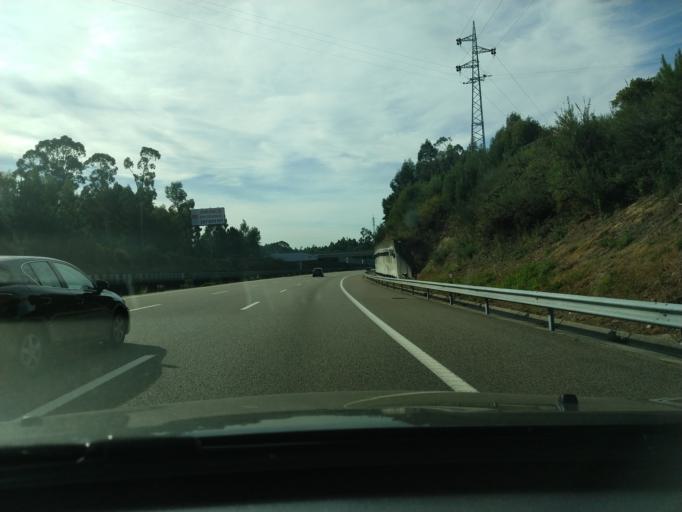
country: PT
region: Aveiro
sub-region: Santa Maria da Feira
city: Rio Meao
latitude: 40.9634
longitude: -8.5677
